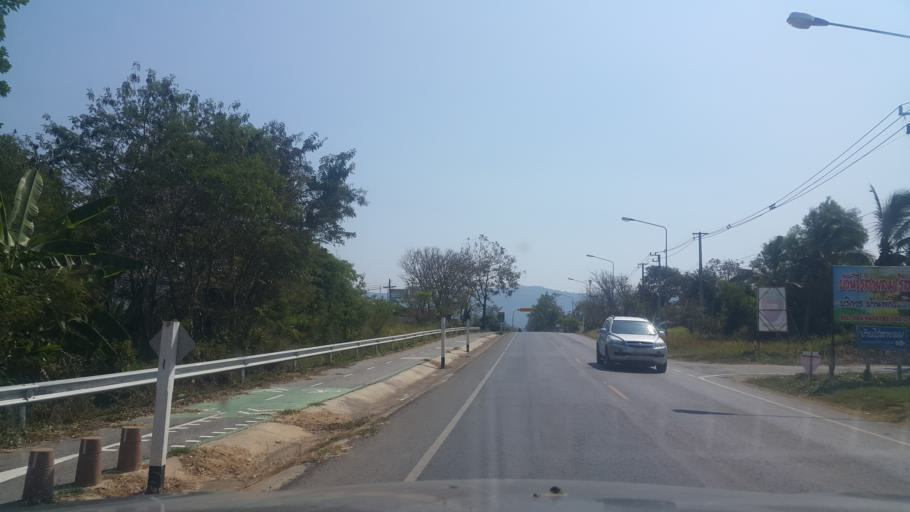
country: TH
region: Nakhon Ratchasima
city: Wang Nam Khiao
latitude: 14.3637
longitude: 101.9121
